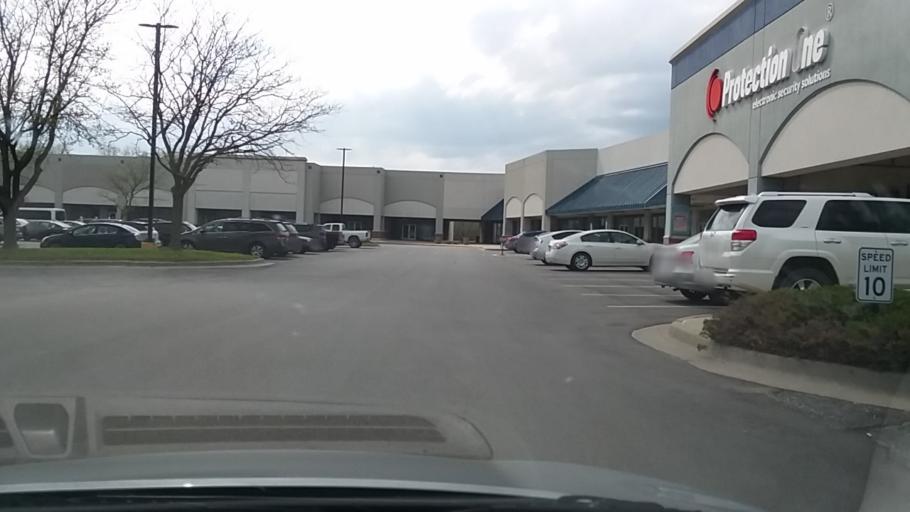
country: US
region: Kansas
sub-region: Douglas County
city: Lawrence
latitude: 38.9915
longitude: -95.2338
